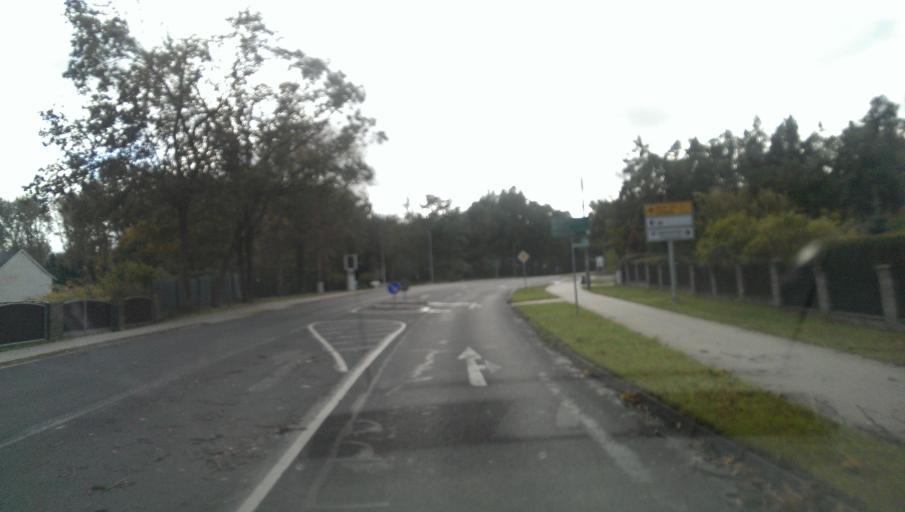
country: DE
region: Brandenburg
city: Luckenwalde
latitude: 52.0764
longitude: 13.1586
